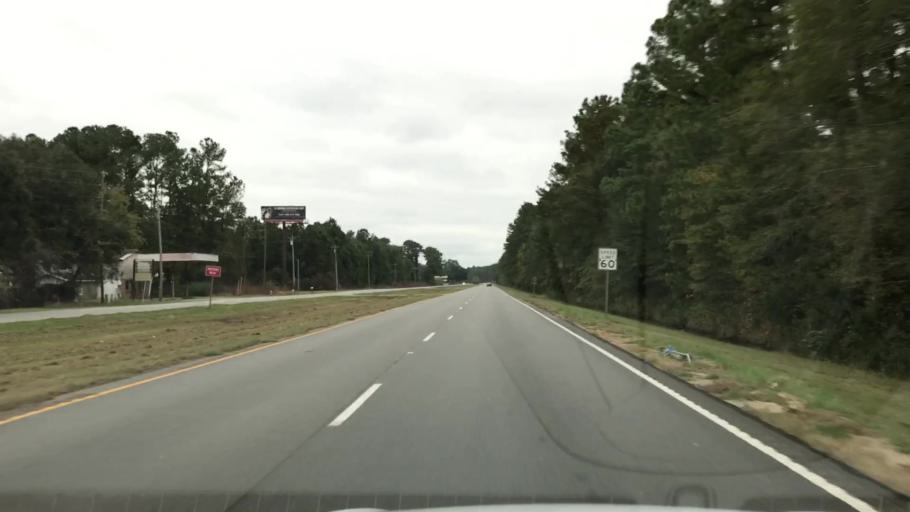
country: US
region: South Carolina
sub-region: Georgetown County
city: Georgetown
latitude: 33.2218
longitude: -79.3787
